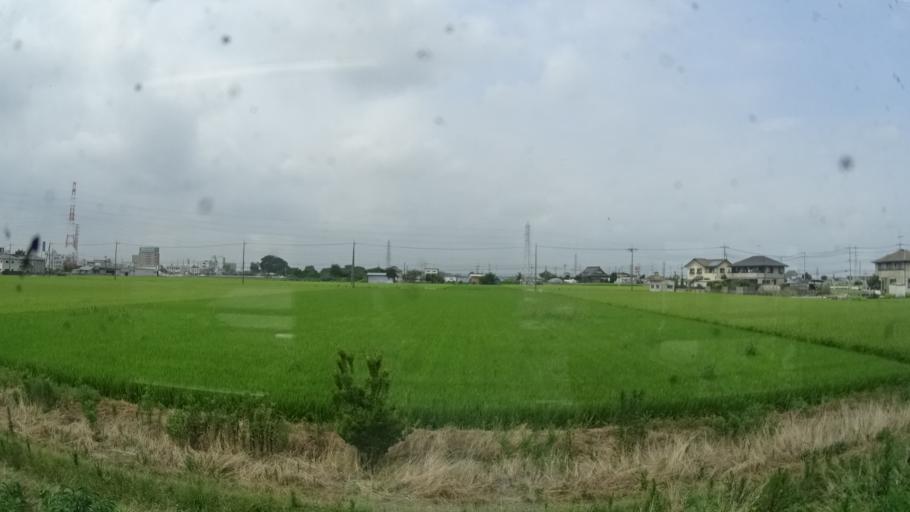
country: JP
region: Ibaraki
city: Shimodate
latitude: 36.3129
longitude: 139.9720
